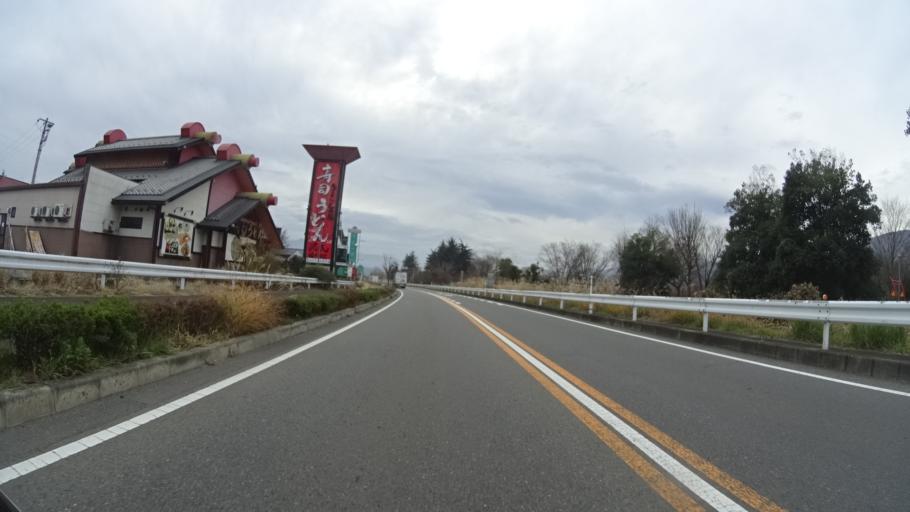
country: JP
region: Gunma
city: Numata
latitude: 36.6514
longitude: 139.0230
